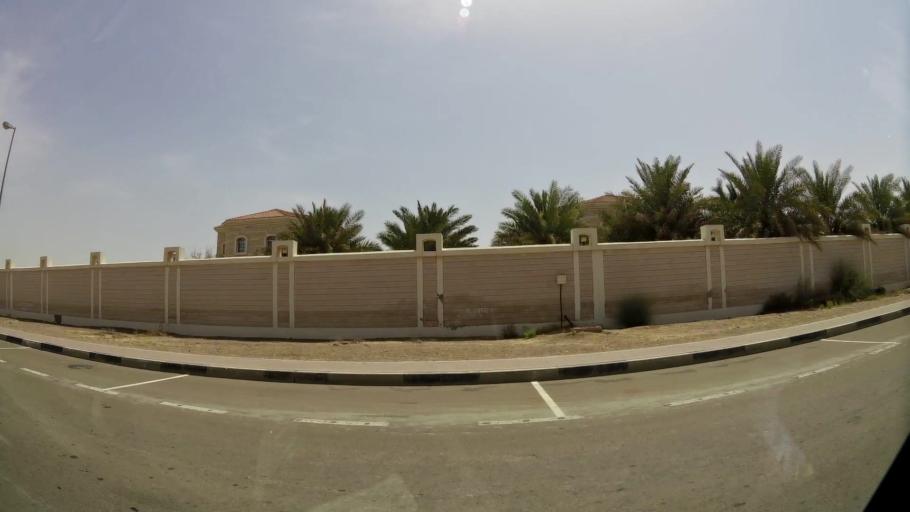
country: AE
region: Abu Dhabi
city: Al Ain
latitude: 24.1755
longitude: 55.7193
